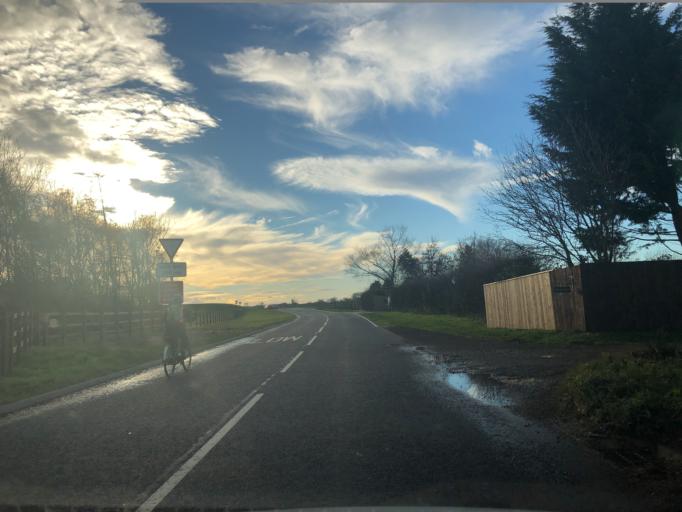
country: GB
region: England
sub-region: North Yorkshire
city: Thirsk
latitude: 54.1801
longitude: -1.3688
